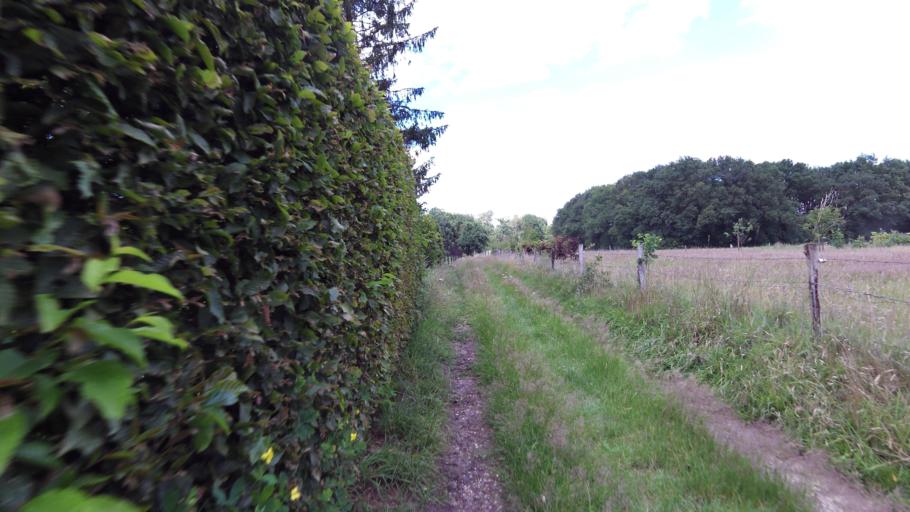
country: NL
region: Gelderland
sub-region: Gemeente Epe
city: Vaassen
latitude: 52.2590
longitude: 5.9329
